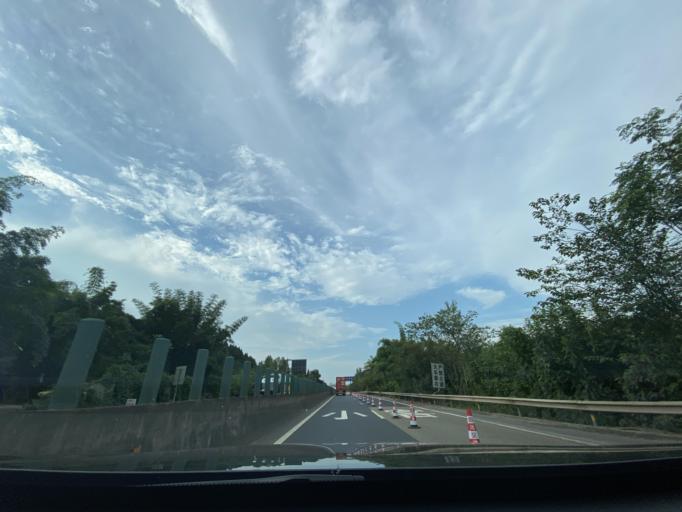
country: CN
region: Sichuan
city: Yanjiang
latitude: 30.0622
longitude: 104.5975
